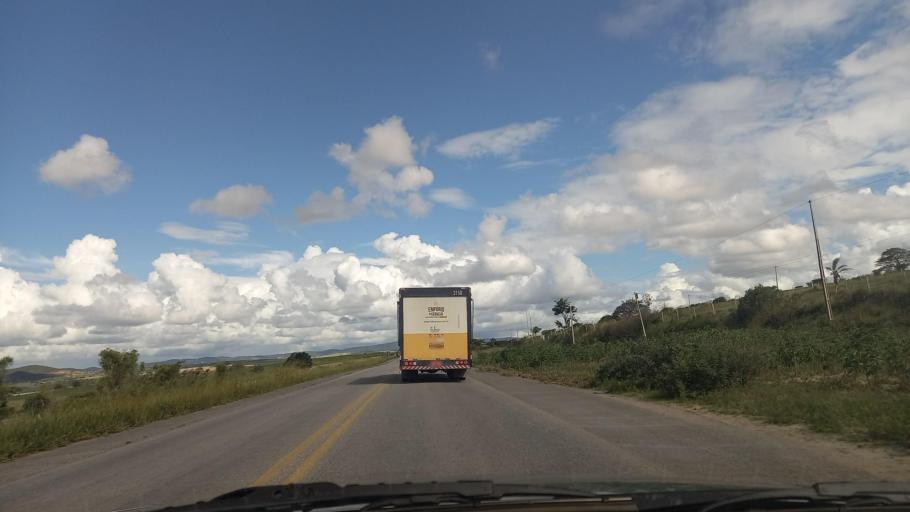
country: BR
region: Pernambuco
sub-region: Sao Joao
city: Sao Joao
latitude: -8.7698
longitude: -36.4277
